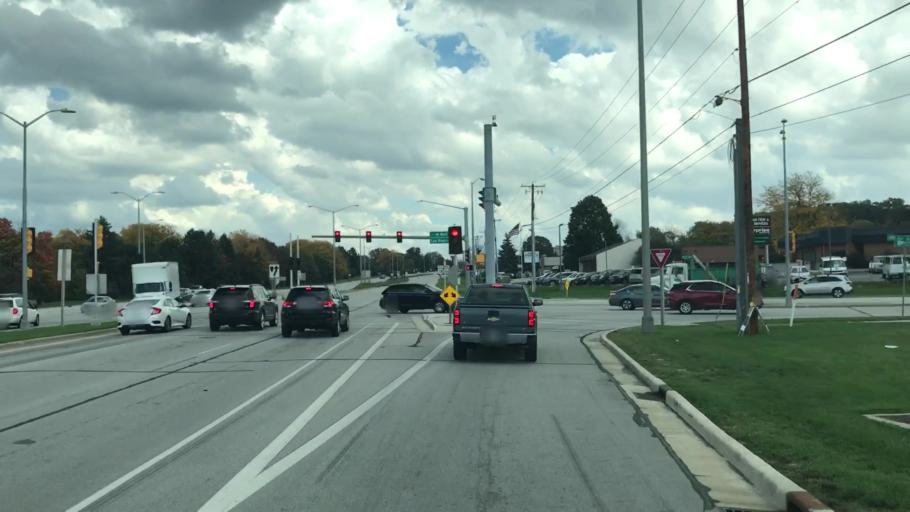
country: US
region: Wisconsin
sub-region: Waukesha County
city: Waukesha
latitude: 43.0257
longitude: -88.2009
